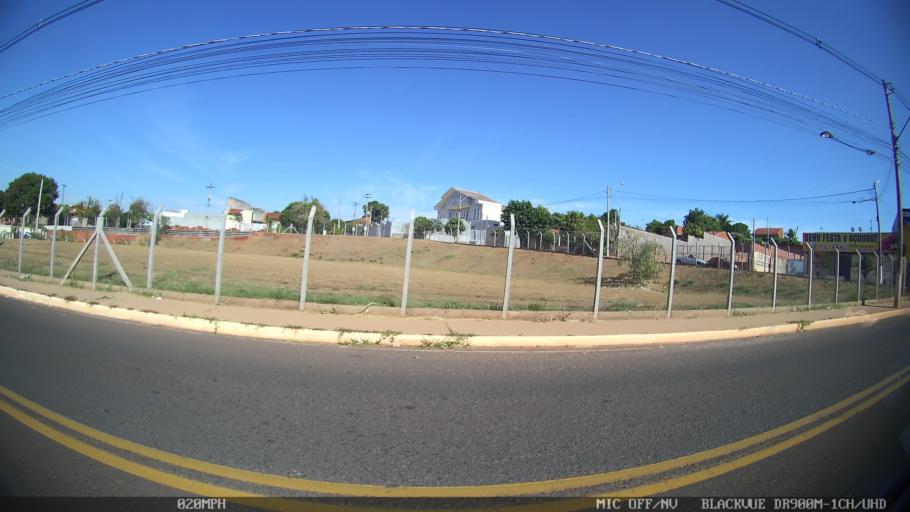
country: BR
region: Sao Paulo
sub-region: Sao Jose Do Rio Preto
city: Sao Jose do Rio Preto
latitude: -20.7691
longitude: -49.4187
